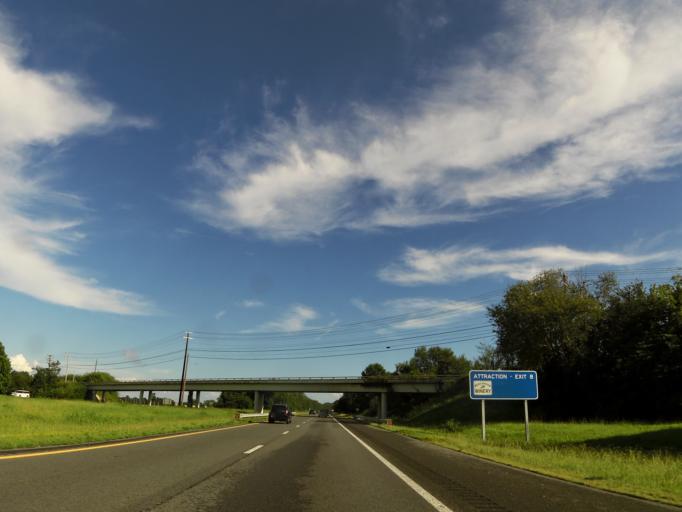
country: US
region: Tennessee
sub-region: Montgomery County
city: Clarksville
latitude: 36.5802
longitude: -87.2658
